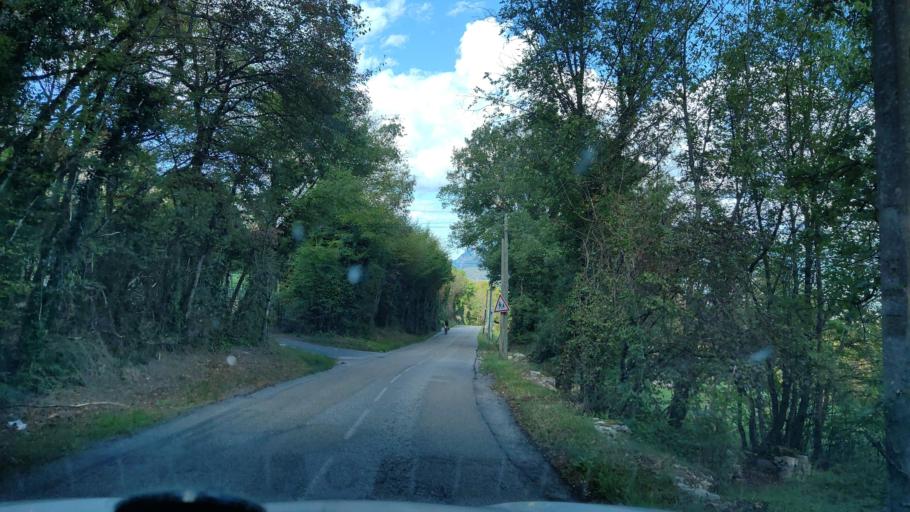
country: FR
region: Rhone-Alpes
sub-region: Departement de la Savoie
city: Jacob-Bellecombette
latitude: 45.5409
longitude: 5.9131
